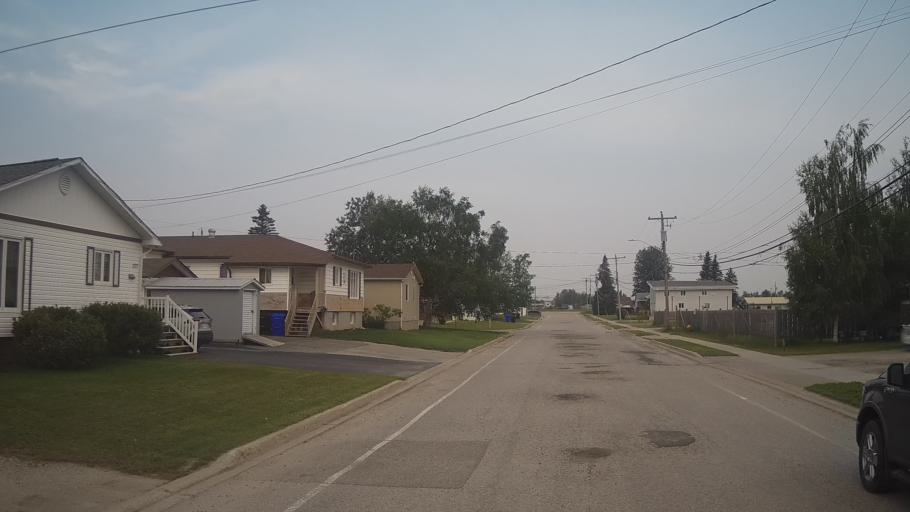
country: CA
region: Ontario
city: Hearst
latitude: 49.6893
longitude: -83.6506
